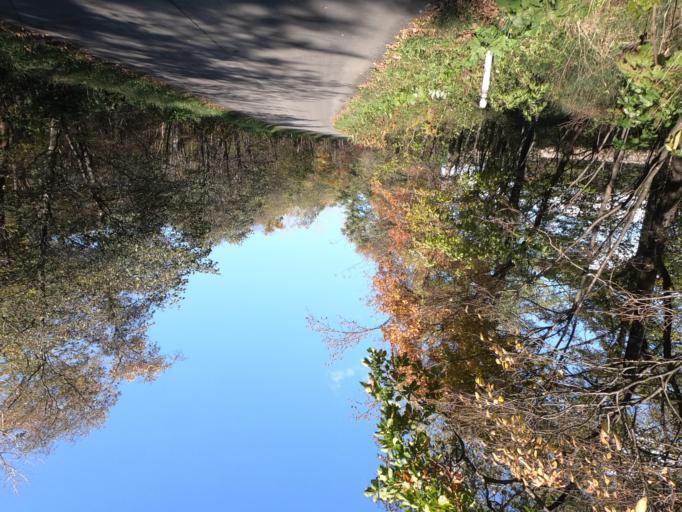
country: JP
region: Hokkaido
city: Otofuke
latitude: 43.2324
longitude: 143.2636
